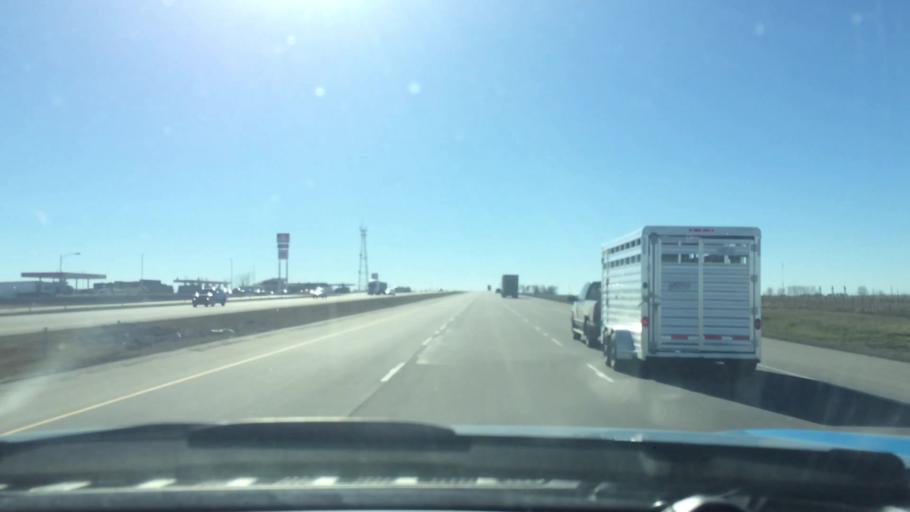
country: CA
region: Alberta
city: Crossfield
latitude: 51.4168
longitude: -114.0020
